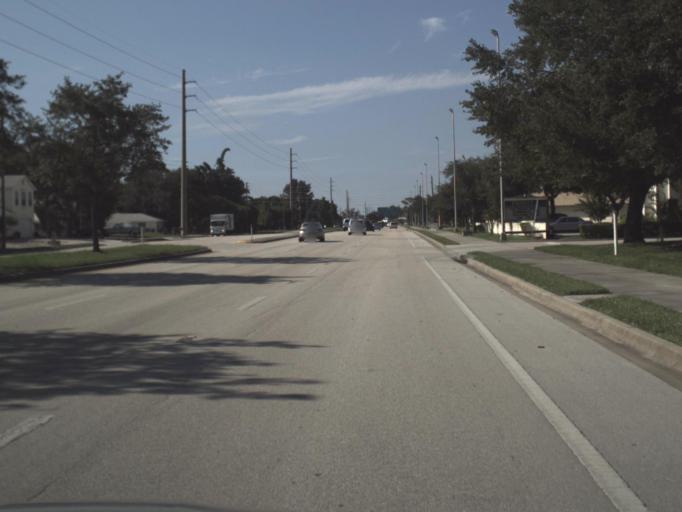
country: US
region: Florida
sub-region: Sarasota County
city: South Venice
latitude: 27.0442
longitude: -82.4023
